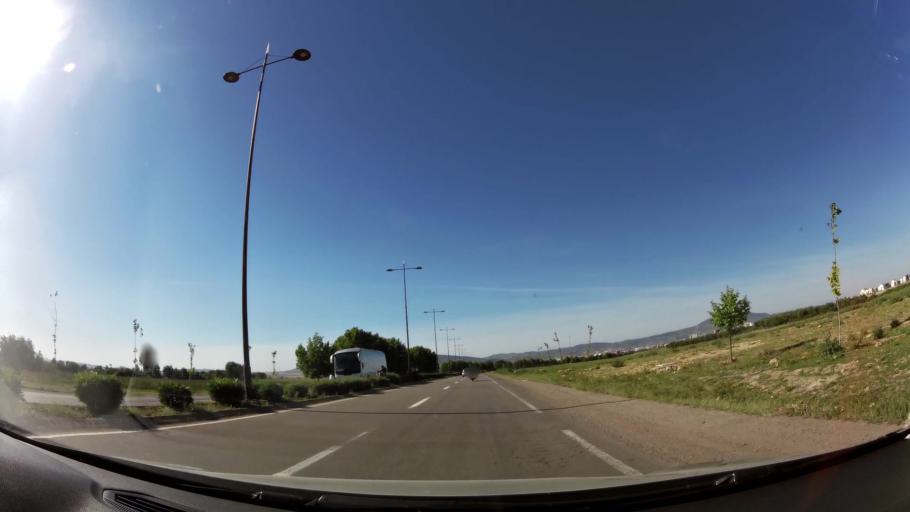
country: MA
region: Fes-Boulemane
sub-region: Fes
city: Fes
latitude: 33.9947
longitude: -5.0243
